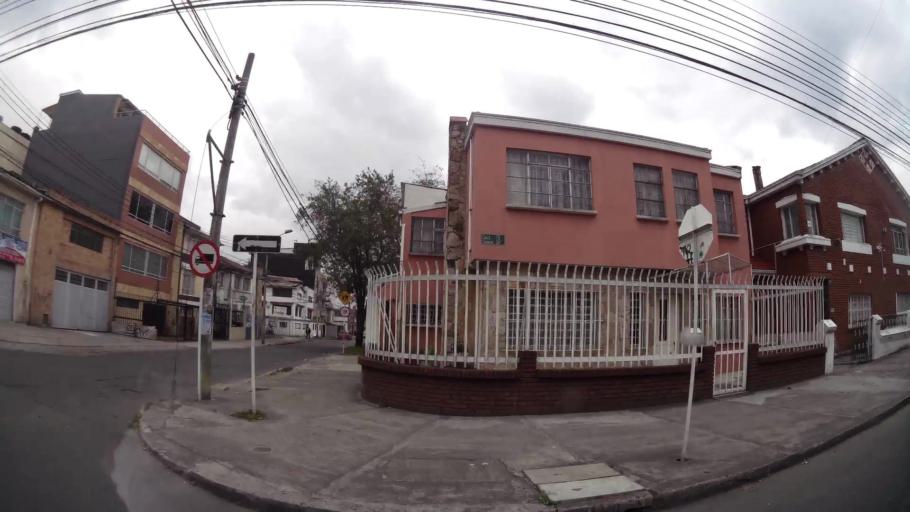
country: CO
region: Bogota D.C.
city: Barrio San Luis
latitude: 4.6641
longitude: -74.0630
